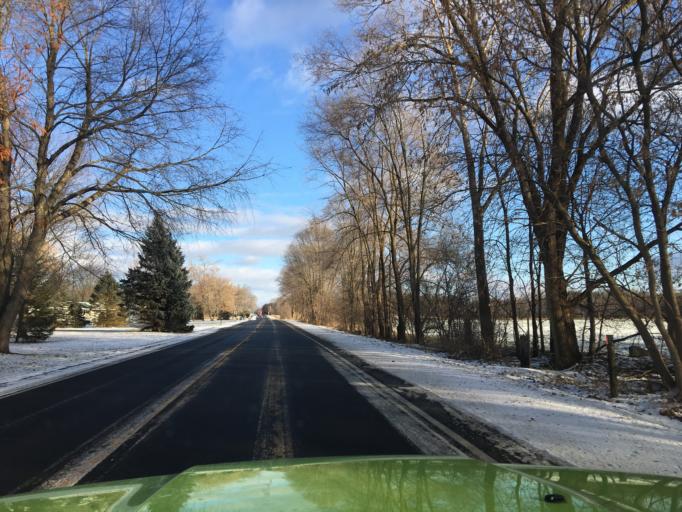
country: US
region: Michigan
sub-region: Montcalm County
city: Greenville
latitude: 43.2063
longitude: -85.2631
